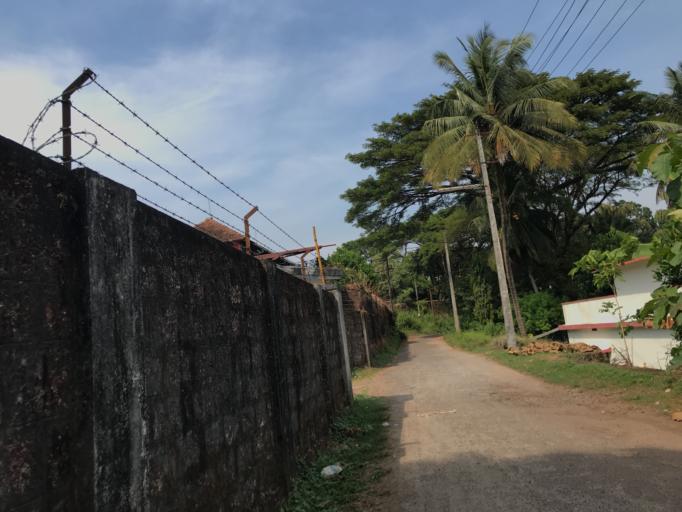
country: IN
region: Karnataka
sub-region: Dakshina Kannada
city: Ullal
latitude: 12.8437
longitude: 74.8515
